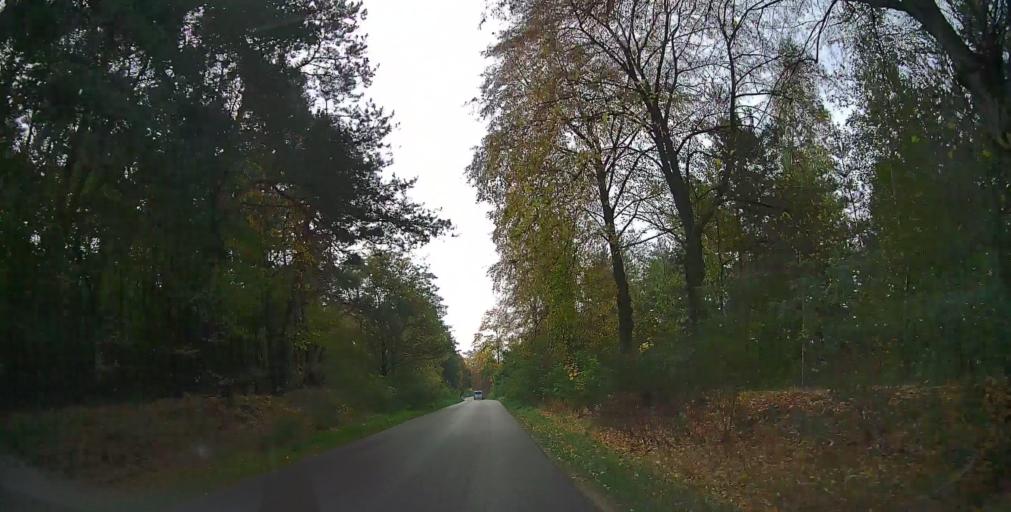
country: PL
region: Masovian Voivodeship
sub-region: Powiat grojecki
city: Mogielnica
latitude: 51.6717
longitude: 20.7119
